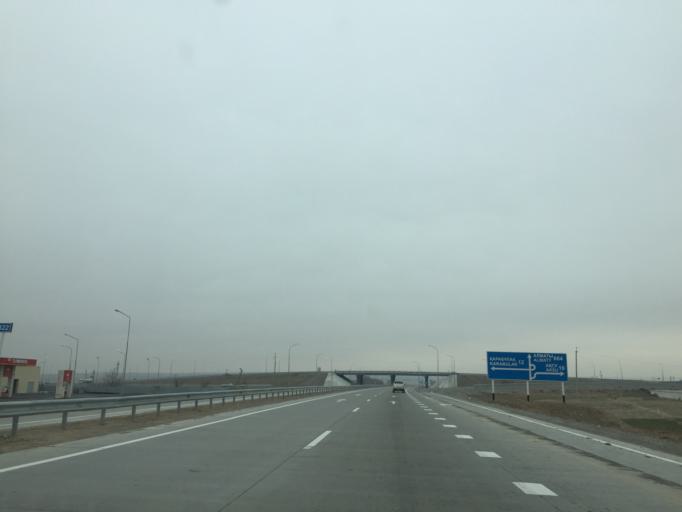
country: KZ
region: Ongtustik Qazaqstan
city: Aksu
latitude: 42.4727
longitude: 69.8110
